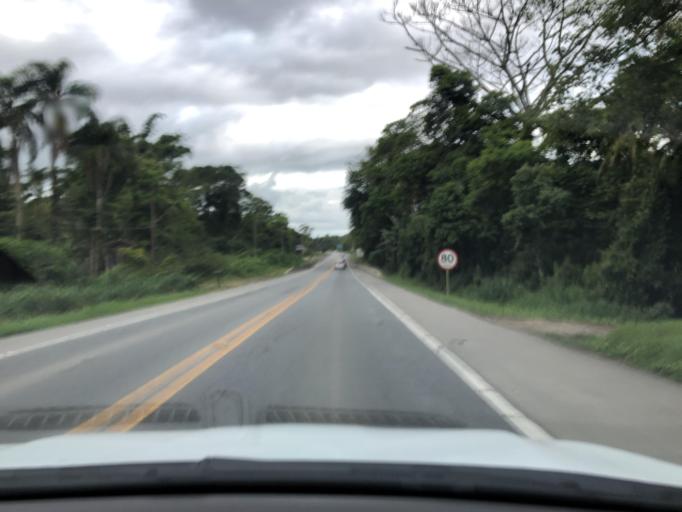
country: BR
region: Santa Catarina
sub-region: Sao Francisco Do Sul
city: Sao Francisco do Sul
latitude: -26.3065
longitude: -48.6417
